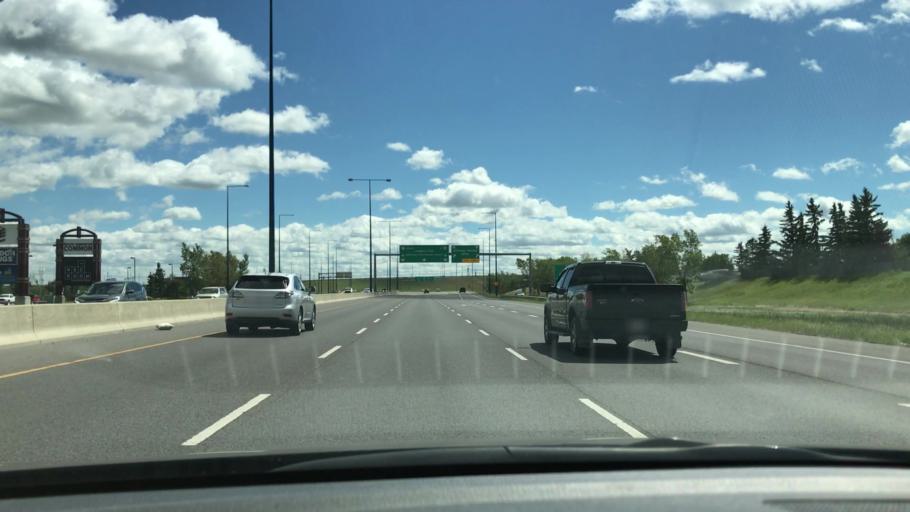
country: CA
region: Alberta
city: Edmonton
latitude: 53.4456
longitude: -113.4928
